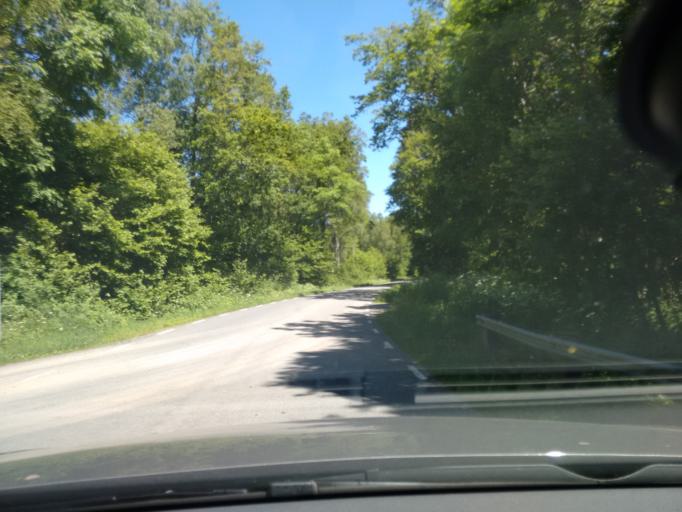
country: SE
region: Skane
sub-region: Kristianstads Kommun
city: Degeberga
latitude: 55.7683
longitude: 14.0021
